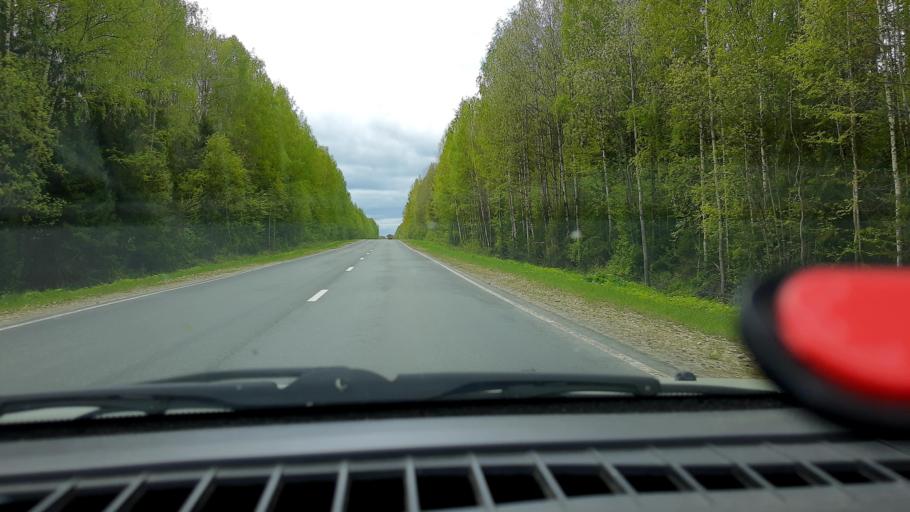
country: RU
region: Nizjnij Novgorod
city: Uren'
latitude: 57.2307
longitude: 45.5431
